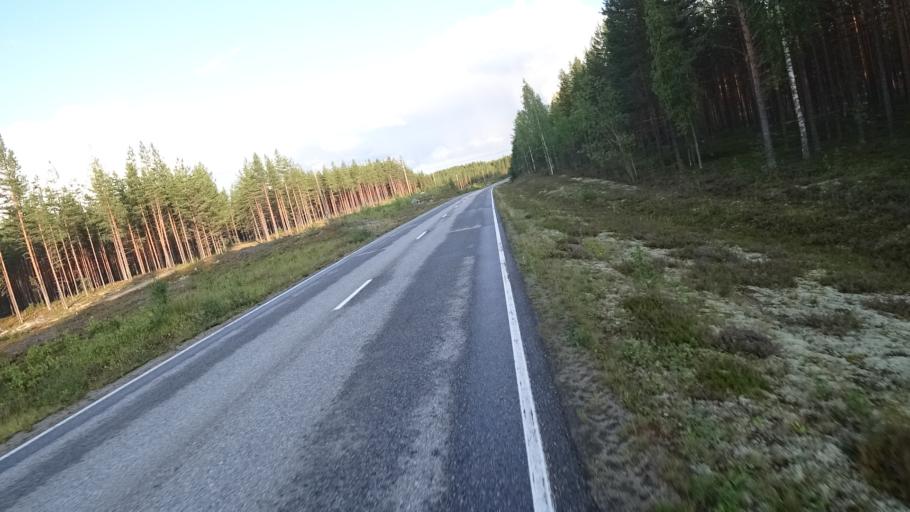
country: FI
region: North Karelia
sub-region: Joensuu
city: Ilomantsi
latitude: 62.6370
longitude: 31.0865
